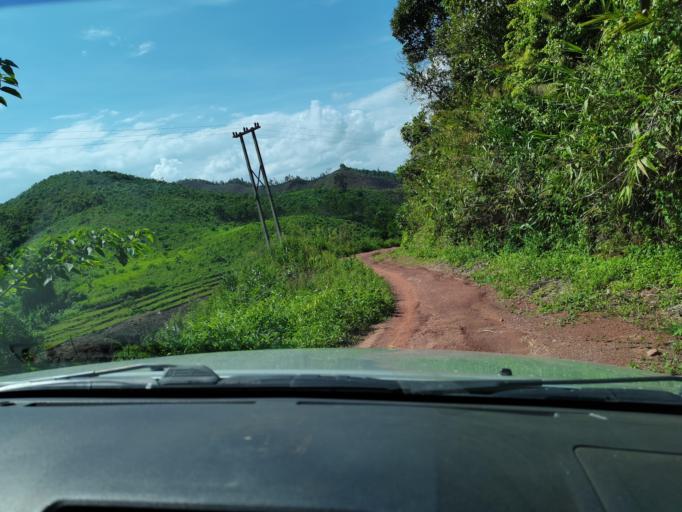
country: LA
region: Loungnamtha
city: Muang Nale
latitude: 20.5587
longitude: 101.0583
